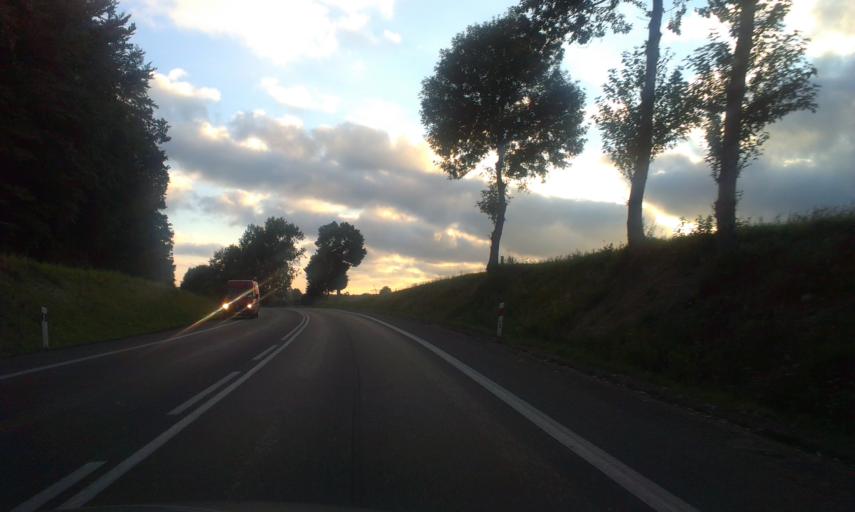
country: PL
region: West Pomeranian Voivodeship
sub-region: Powiat koszalinski
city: Sianow
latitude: 54.2540
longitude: 16.3645
